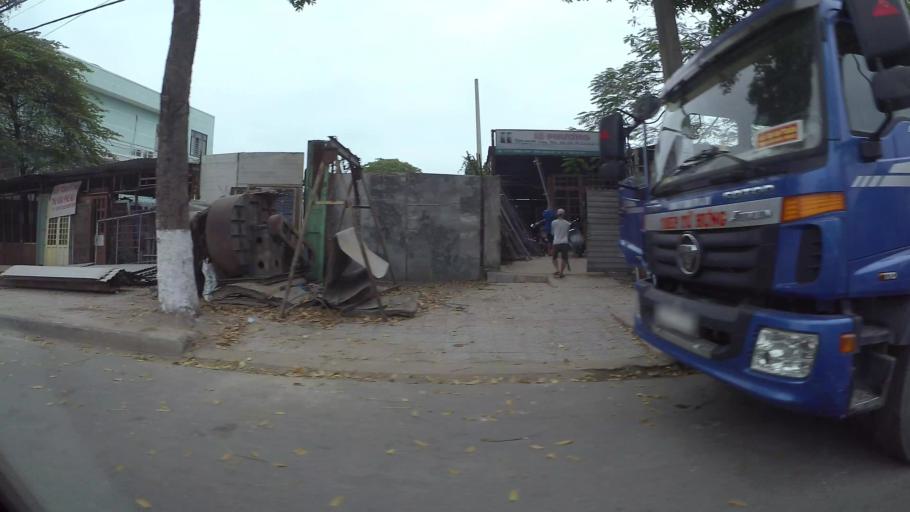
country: VN
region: Da Nang
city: Thanh Khe
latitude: 16.0558
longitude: 108.1809
